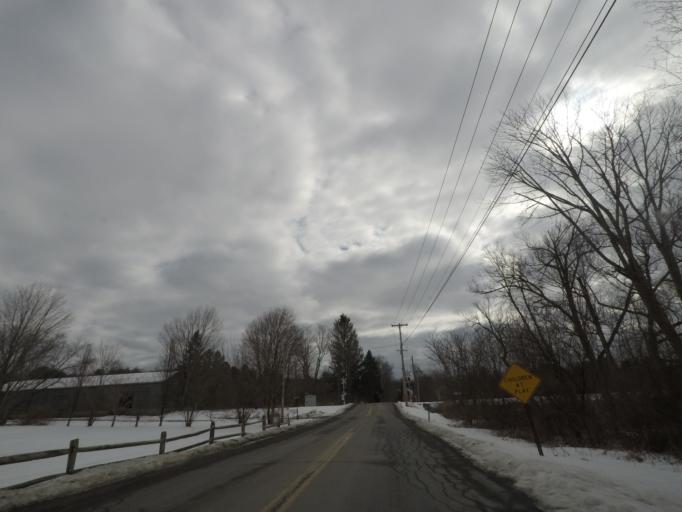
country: US
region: New York
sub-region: Rensselaer County
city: Hoosick Falls
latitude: 42.9450
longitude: -73.4339
